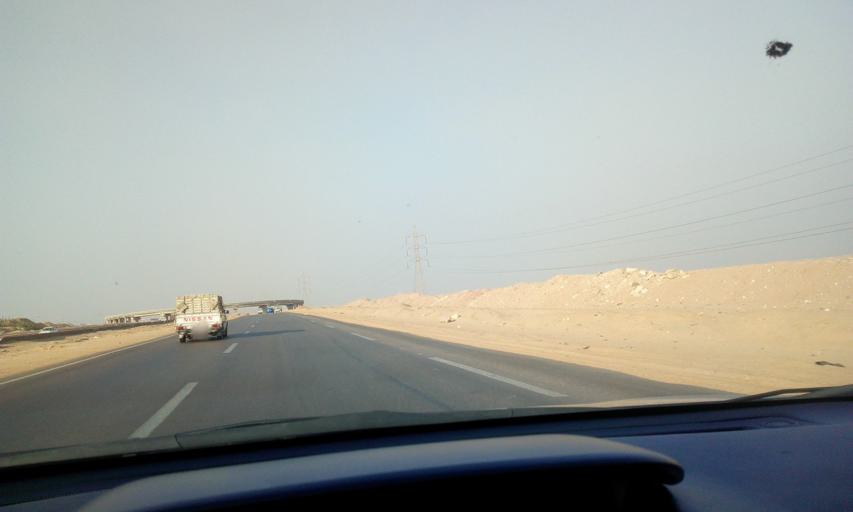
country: EG
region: Al Jizah
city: Madinat Sittah Uktubar
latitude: 29.9214
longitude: 31.0944
